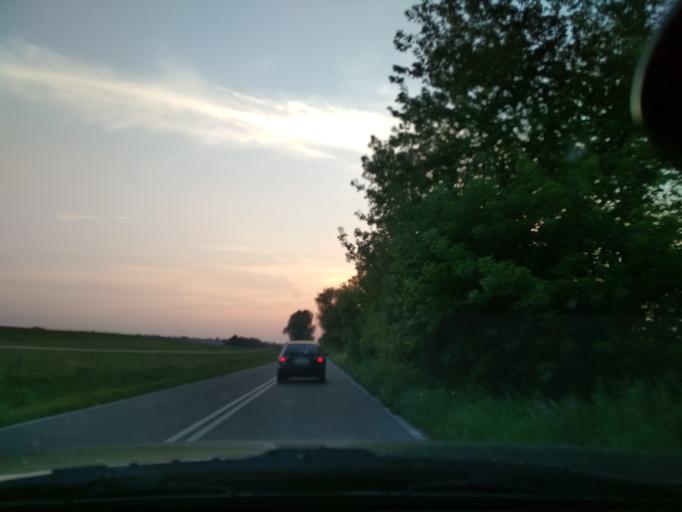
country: PL
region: Lesser Poland Voivodeship
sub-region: Powiat olkuski
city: Wolbrom
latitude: 50.4650
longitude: 19.7758
